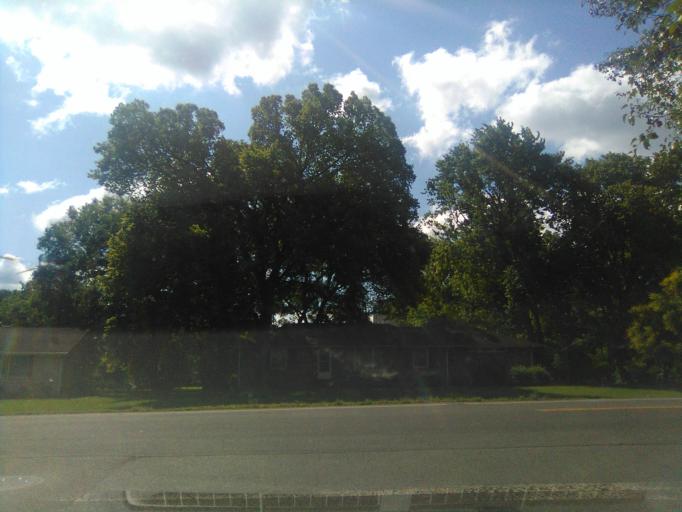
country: US
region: Tennessee
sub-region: Davidson County
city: Belle Meade
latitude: 36.1062
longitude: -86.8693
